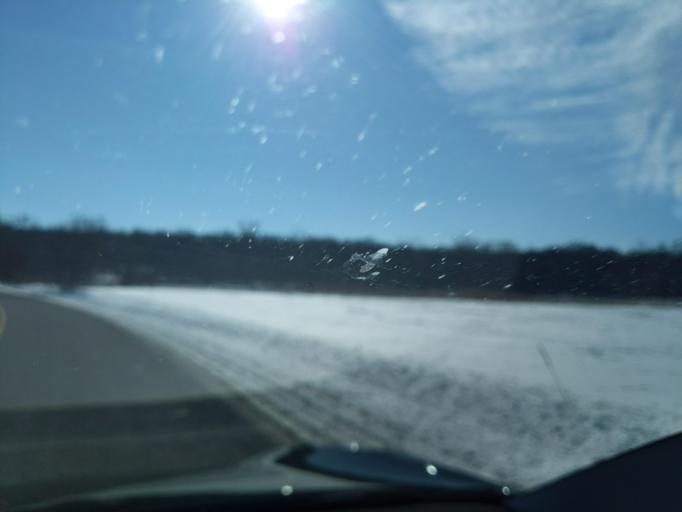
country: US
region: Michigan
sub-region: Ingham County
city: Stockbridge
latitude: 42.4990
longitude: -84.0890
